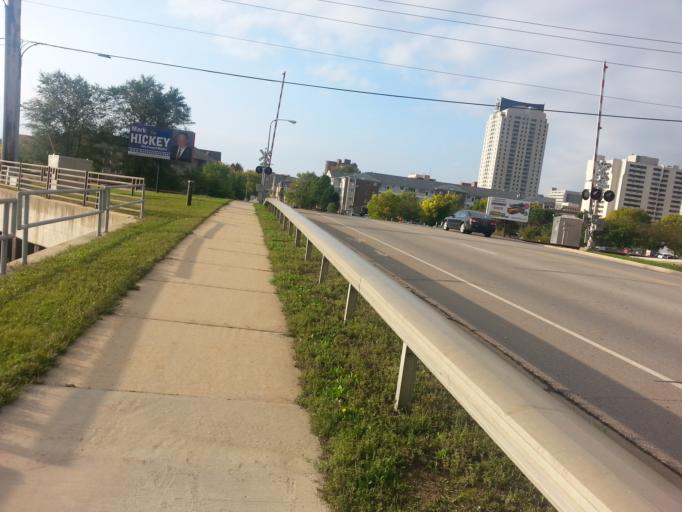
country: US
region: Minnesota
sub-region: Olmsted County
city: Rochester
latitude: 44.0266
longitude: -92.4601
